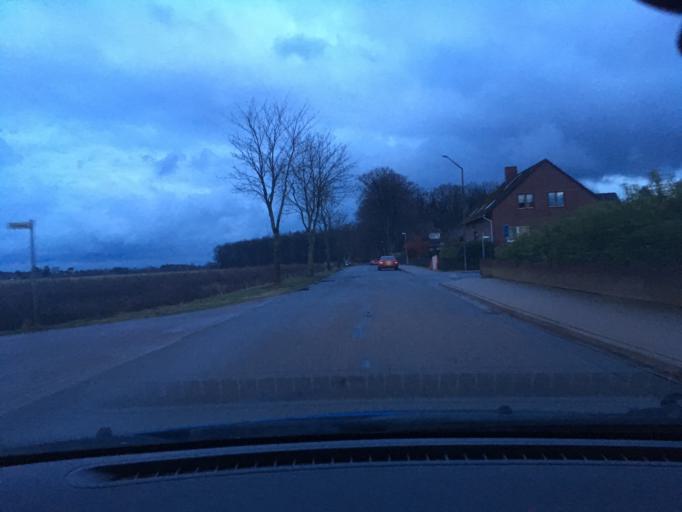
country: DE
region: Lower Saxony
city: Embsen
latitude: 53.1756
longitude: 10.3494
